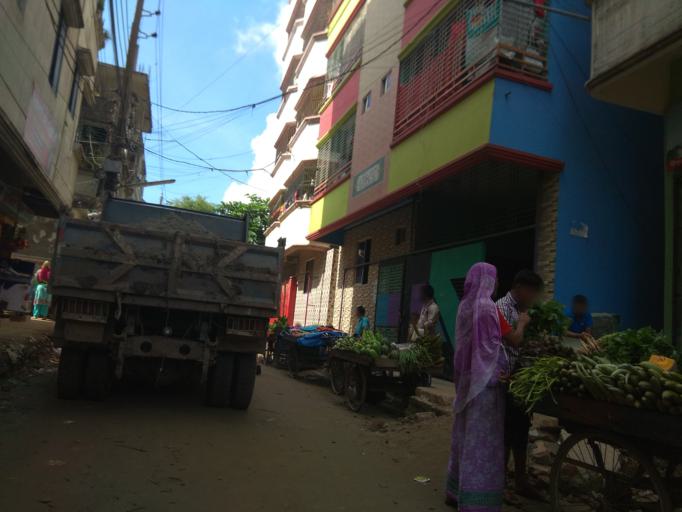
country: BD
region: Dhaka
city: Tungi
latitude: 23.8154
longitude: 90.3870
